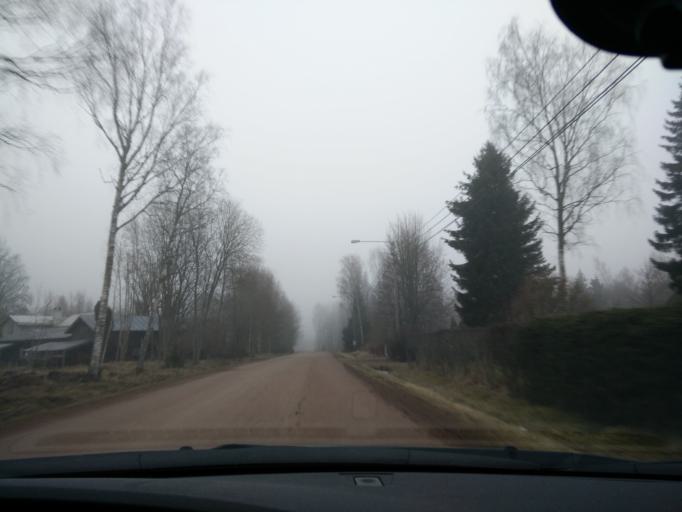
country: AX
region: Mariehamns stad
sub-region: Mariehamn
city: Mariehamn
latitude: 60.1013
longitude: 19.9046
